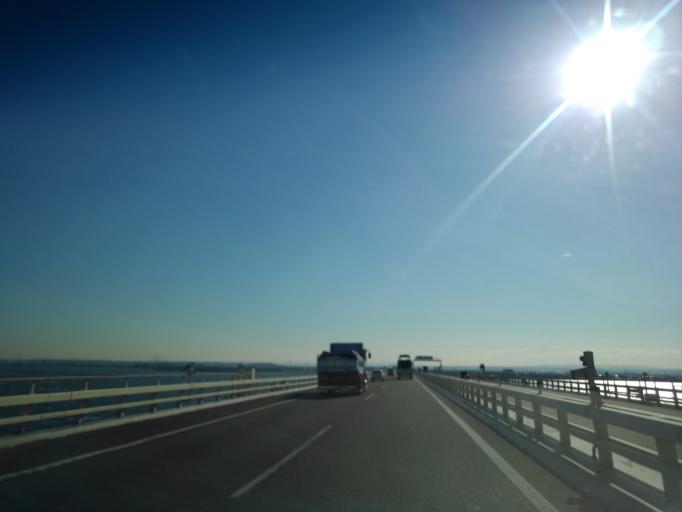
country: JP
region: Chiba
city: Kisarazu
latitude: 35.4448
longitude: 139.9031
